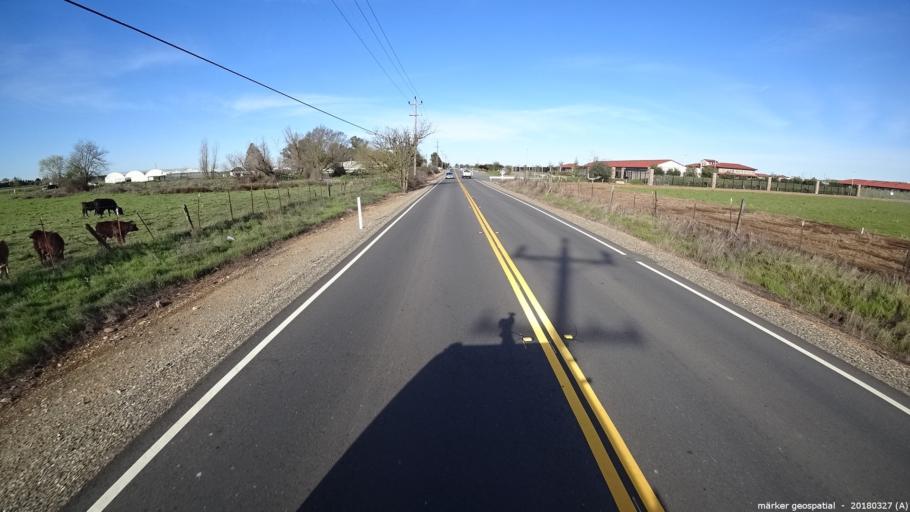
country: US
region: California
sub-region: Sacramento County
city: Vineyard
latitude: 38.4964
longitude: -121.3111
